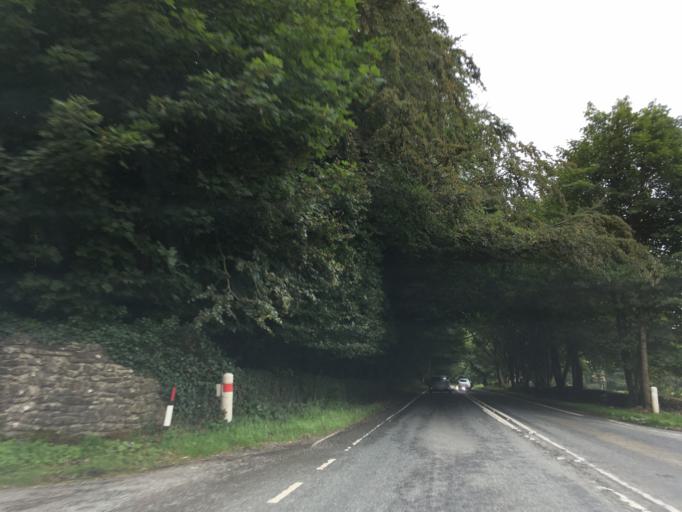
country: GB
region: England
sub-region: Somerset
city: Mendip
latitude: 51.2437
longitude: -2.6117
